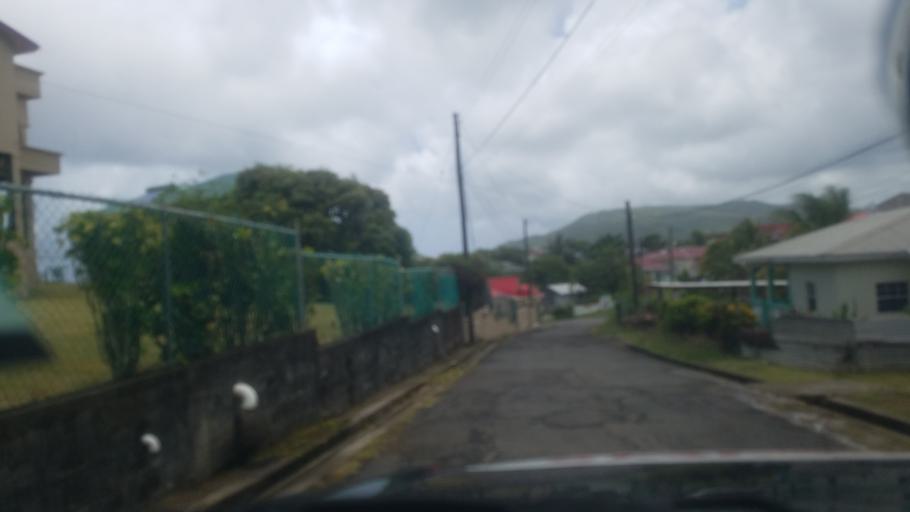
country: LC
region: Laborie Quarter
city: Laborie
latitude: 13.7458
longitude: -60.9669
